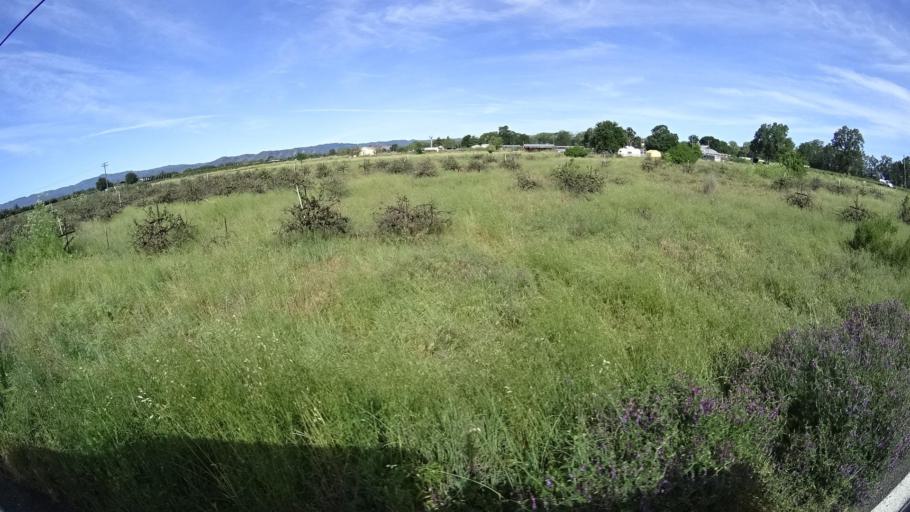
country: US
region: California
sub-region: Lake County
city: Kelseyville
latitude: 39.0101
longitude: -122.8243
